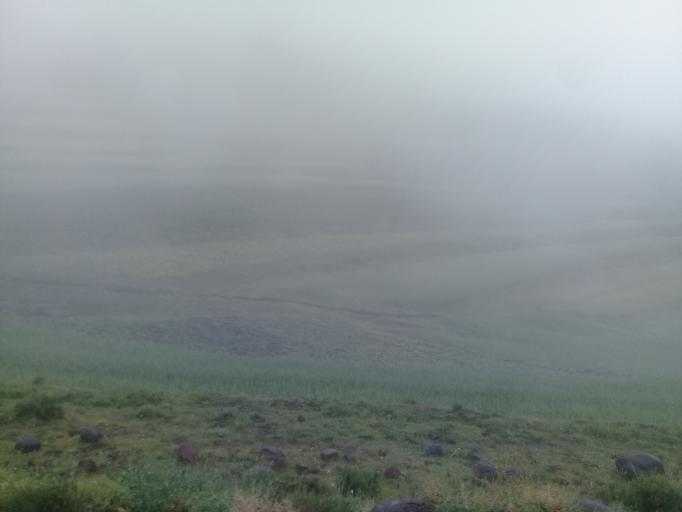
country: LS
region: Mokhotlong
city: Mokhotlong
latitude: -29.3882
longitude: 28.9743
